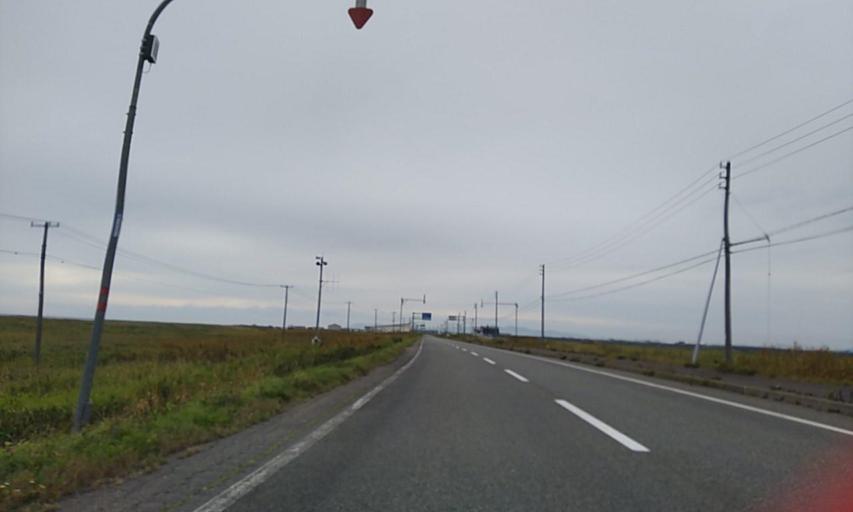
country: JP
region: Hokkaido
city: Makubetsu
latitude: 45.3107
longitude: 142.1942
